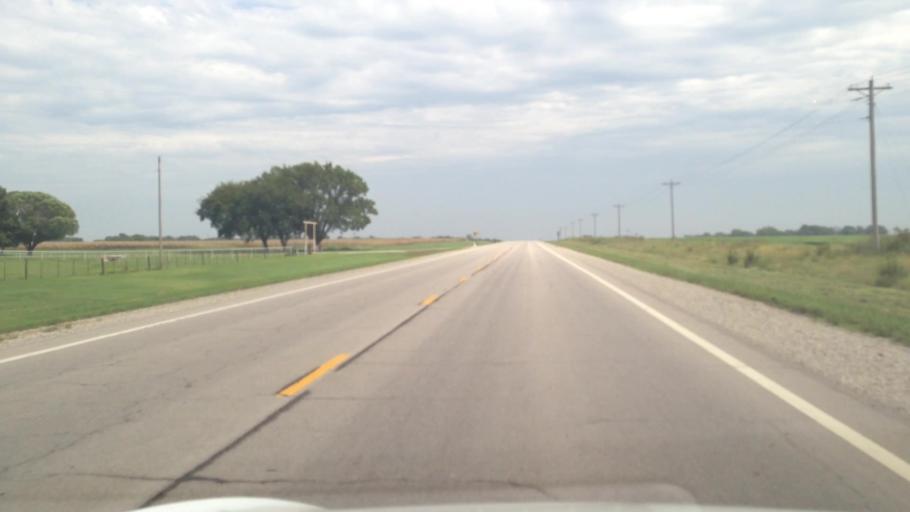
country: US
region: Kansas
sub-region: Crawford County
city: Girard
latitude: 37.5144
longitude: -94.9309
